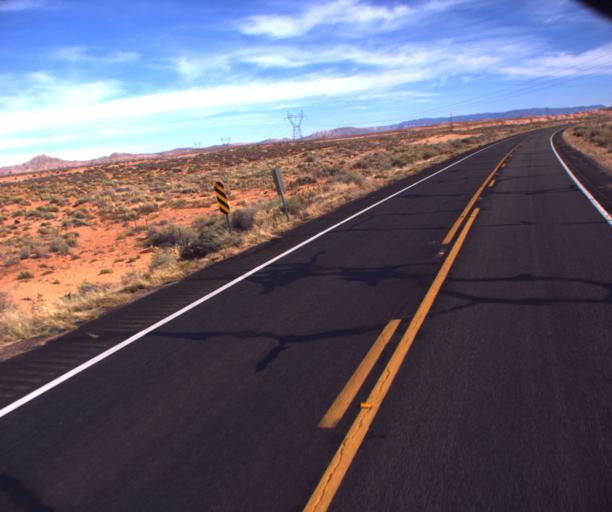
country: US
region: Arizona
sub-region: Apache County
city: Many Farms
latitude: 36.9403
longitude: -109.6424
